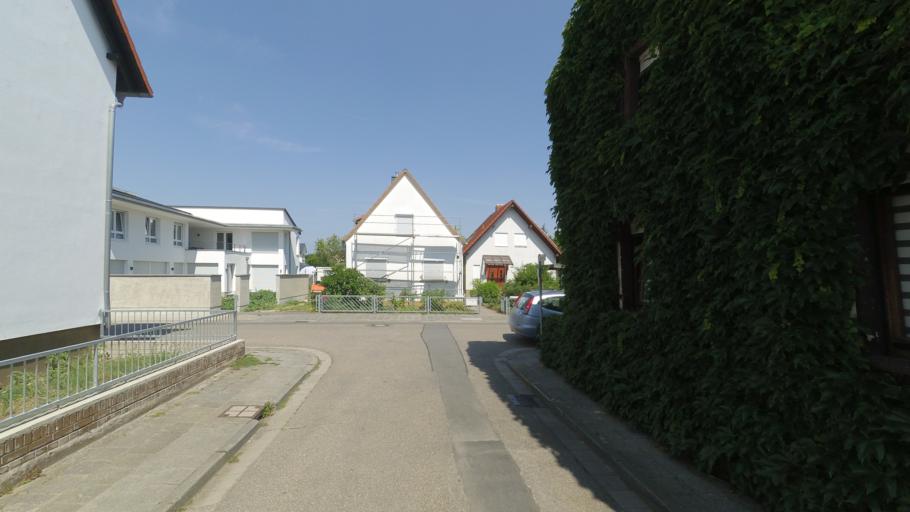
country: DE
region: Rheinland-Pfalz
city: Mutterstadt
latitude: 49.4383
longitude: 8.3630
